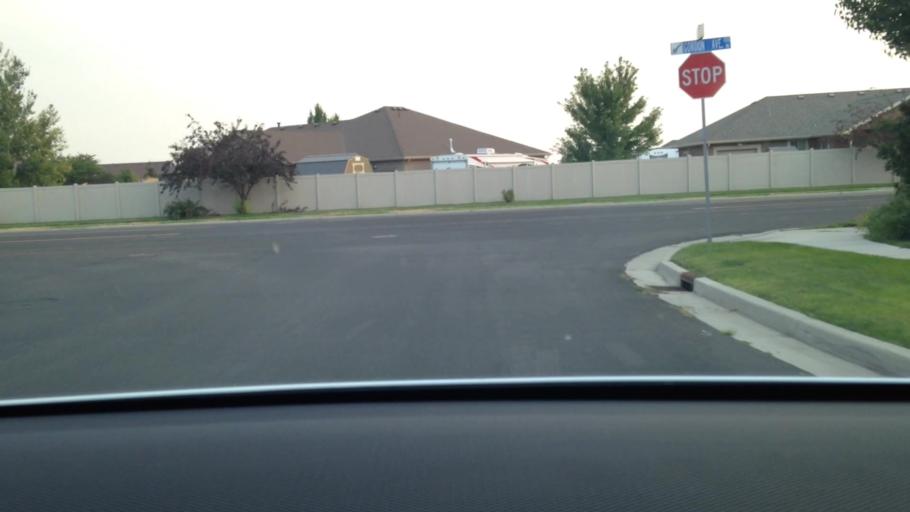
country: US
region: Utah
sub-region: Davis County
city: Clearfield
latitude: 41.0746
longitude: -112.0101
